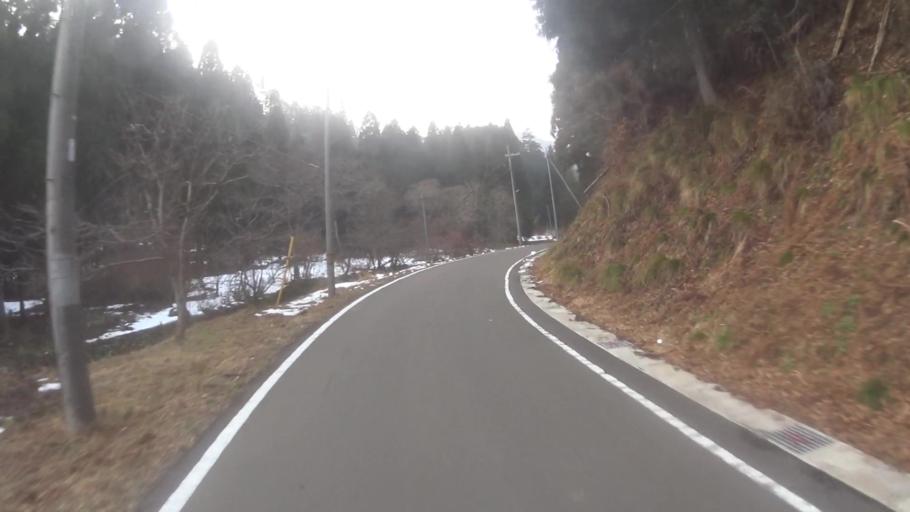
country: JP
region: Kyoto
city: Maizuru
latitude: 35.4325
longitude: 135.4771
